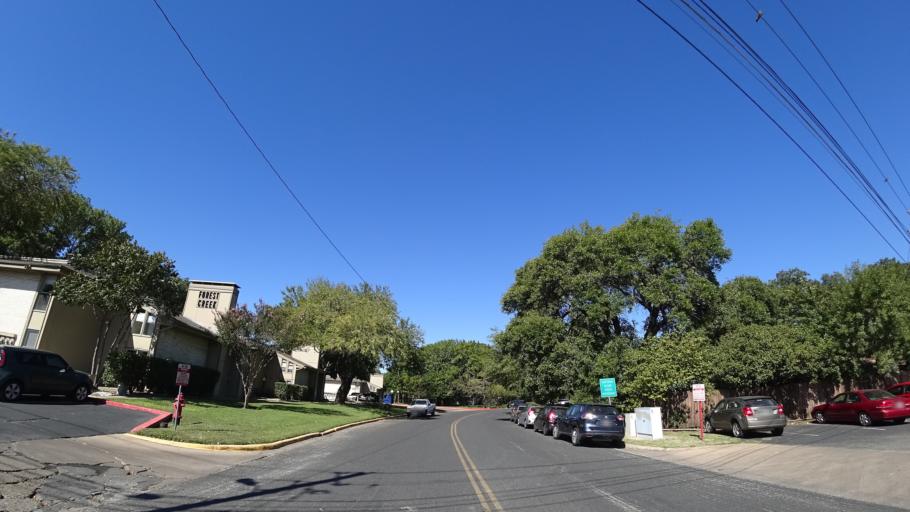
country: US
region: Texas
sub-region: Travis County
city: Austin
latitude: 30.2283
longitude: -97.7459
